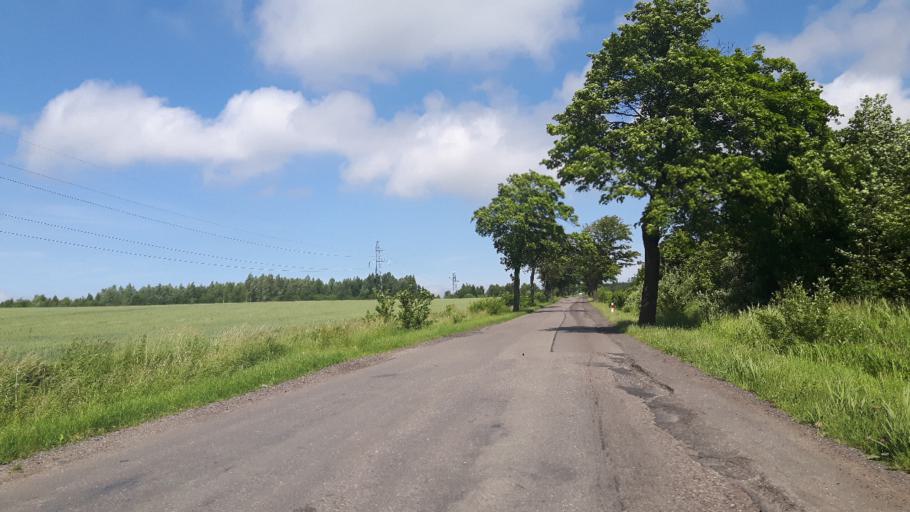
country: PL
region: Pomeranian Voivodeship
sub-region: Powiat slupski
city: Ustka
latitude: 54.5569
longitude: 16.8407
